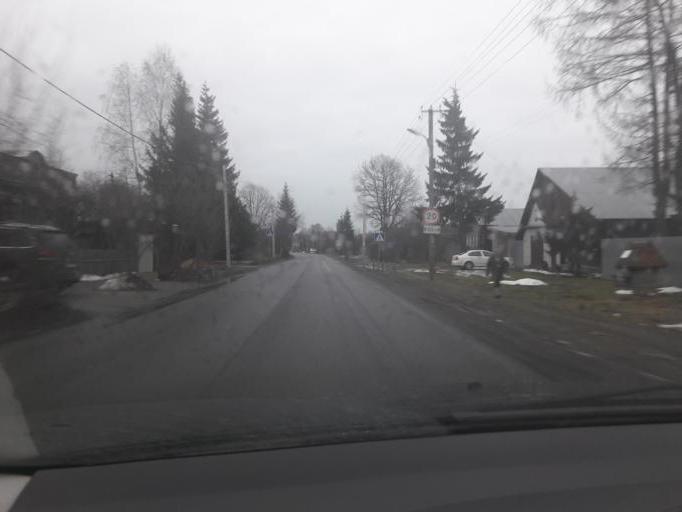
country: RU
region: Moskovskaya
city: Fryazevo
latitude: 55.7512
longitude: 38.5294
